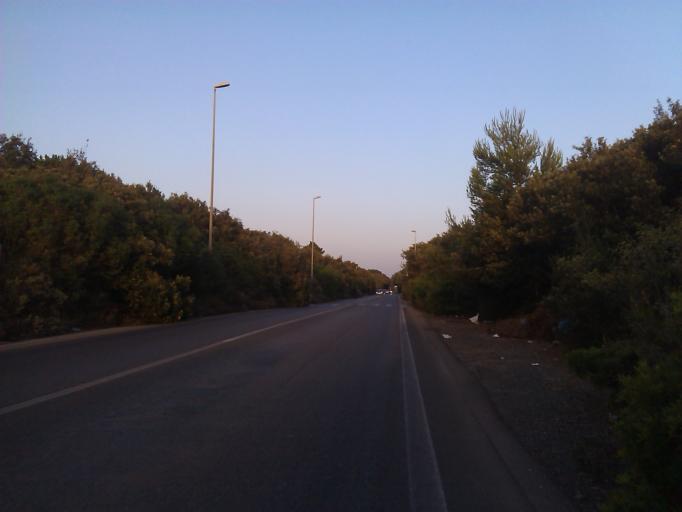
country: IT
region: Latium
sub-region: Citta metropolitana di Roma Capitale
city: Acilia-Castel Fusano-Ostia Antica
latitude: 41.7095
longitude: 12.3321
